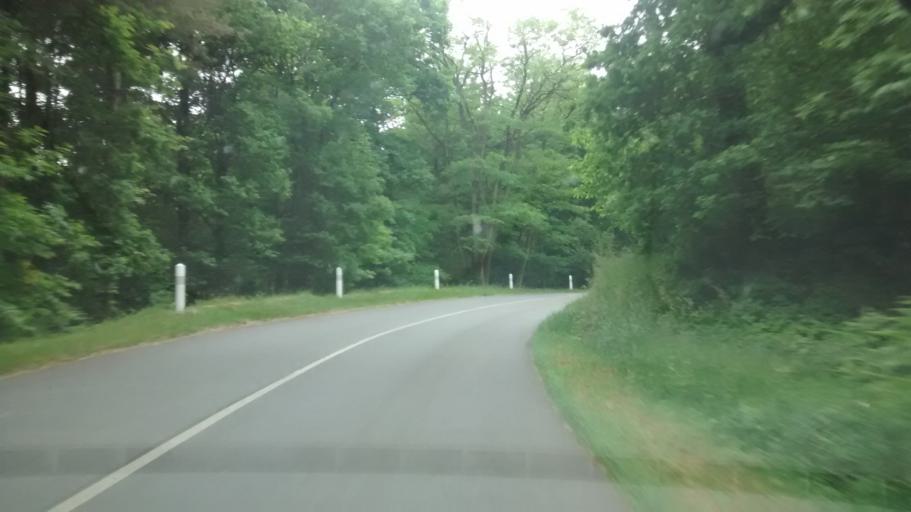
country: FR
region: Brittany
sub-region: Departement du Morbihan
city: Molac
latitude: 47.7802
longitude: -2.4268
